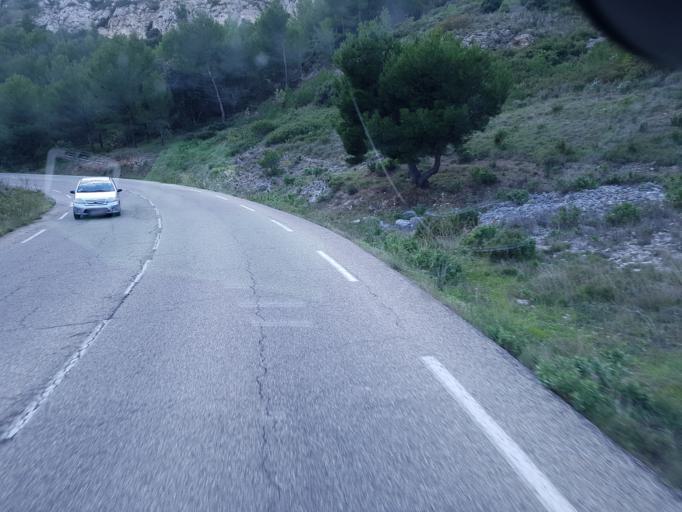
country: FR
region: Provence-Alpes-Cote d'Azur
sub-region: Departement des Bouches-du-Rhone
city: Le Rove
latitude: 43.3517
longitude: 5.2383
